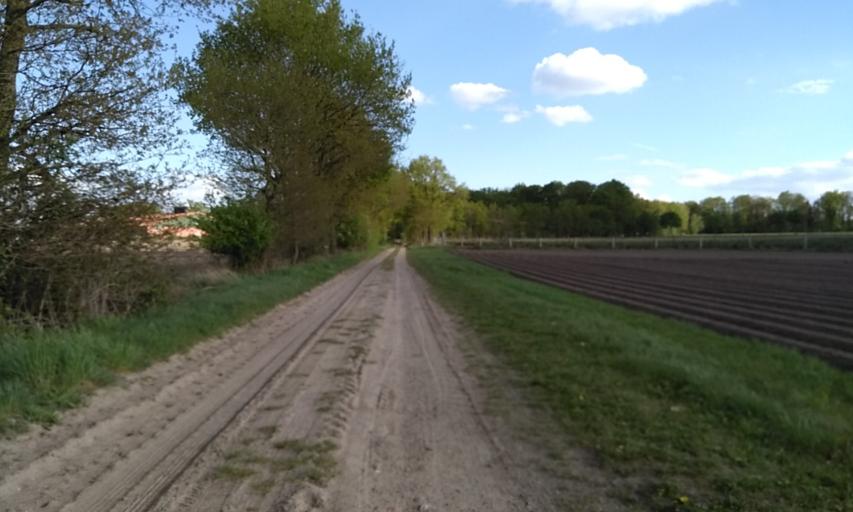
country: DE
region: Lower Saxony
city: Regesbostel
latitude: 53.4071
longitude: 9.6555
